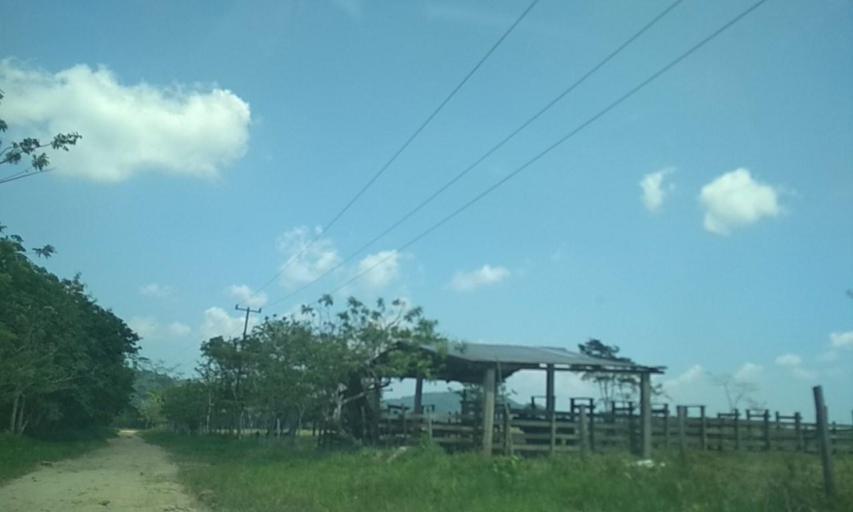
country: MX
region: Chiapas
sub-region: Tecpatan
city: Raudales Malpaso
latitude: 17.3003
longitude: -93.8181
